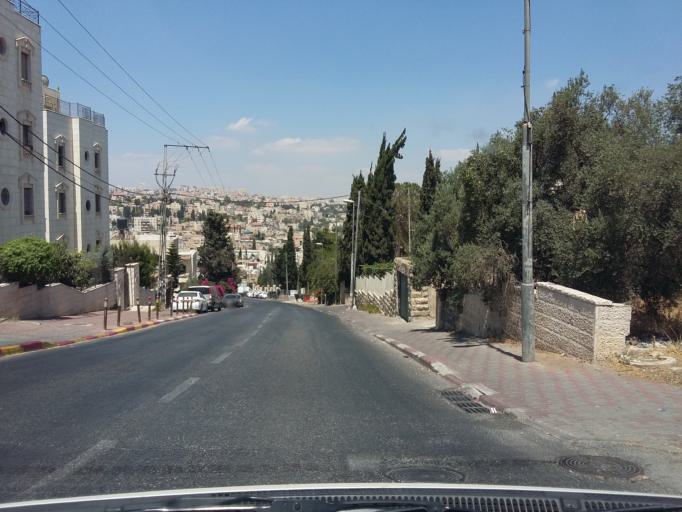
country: PS
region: West Bank
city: East Jerusalem
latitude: 31.7852
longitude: 35.2459
